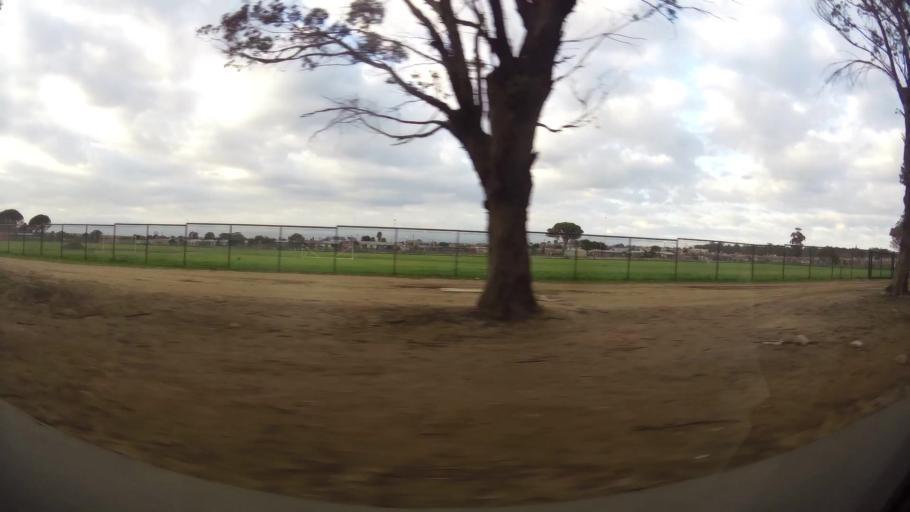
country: ZA
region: Eastern Cape
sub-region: Nelson Mandela Bay Metropolitan Municipality
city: Port Elizabeth
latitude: -33.9846
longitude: 25.5832
